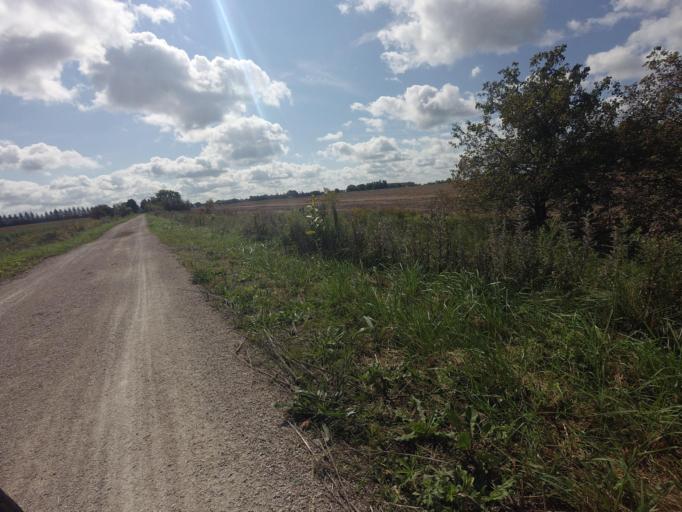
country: CA
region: Ontario
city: Huron East
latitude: 43.6859
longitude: -81.3131
